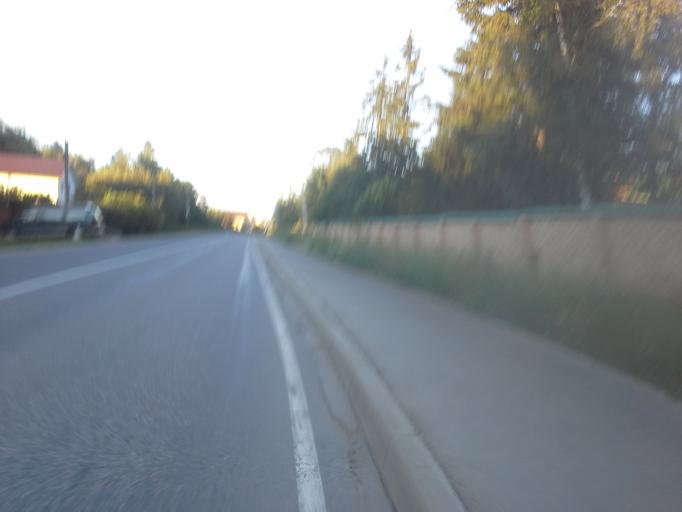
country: RU
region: Moskovskaya
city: Selyatino
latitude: 55.5176
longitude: 36.9478
